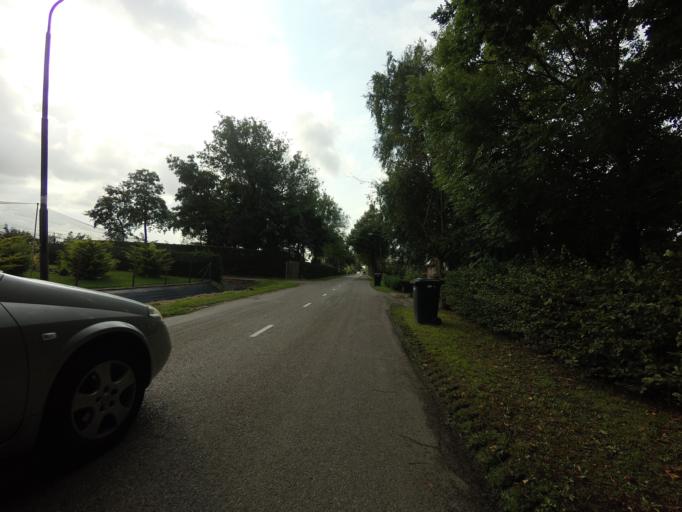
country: NL
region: North Holland
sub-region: Gemeente Hoorn
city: Hoorn
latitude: 52.6997
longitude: 5.0561
